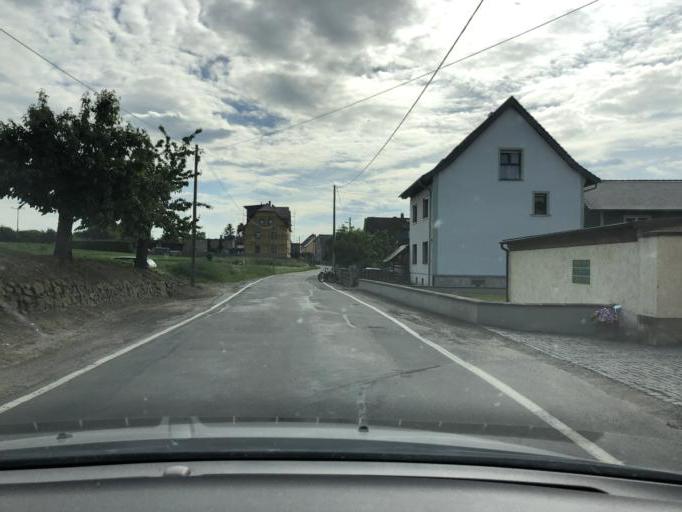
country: DE
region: Saxony
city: Trebsen
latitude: 51.2776
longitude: 12.7249
